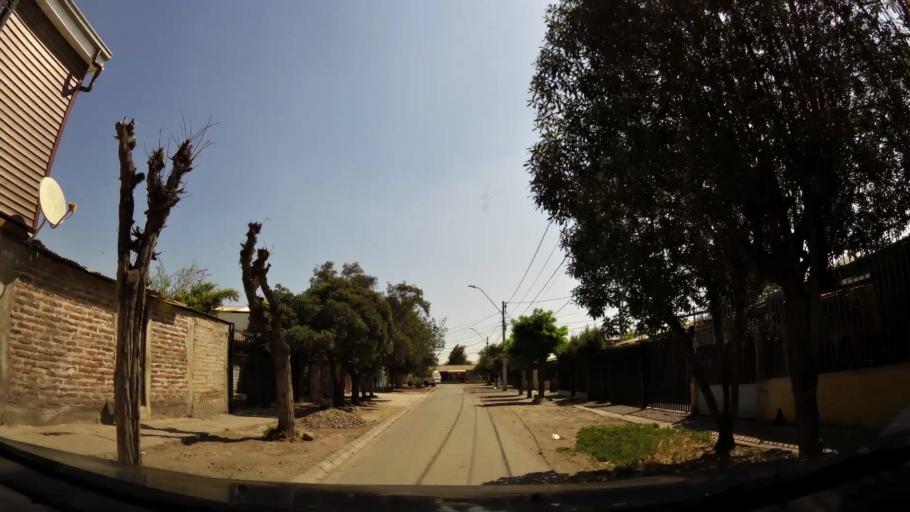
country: CL
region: Santiago Metropolitan
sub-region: Provincia de Maipo
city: San Bernardo
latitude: -33.5783
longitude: -70.7059
